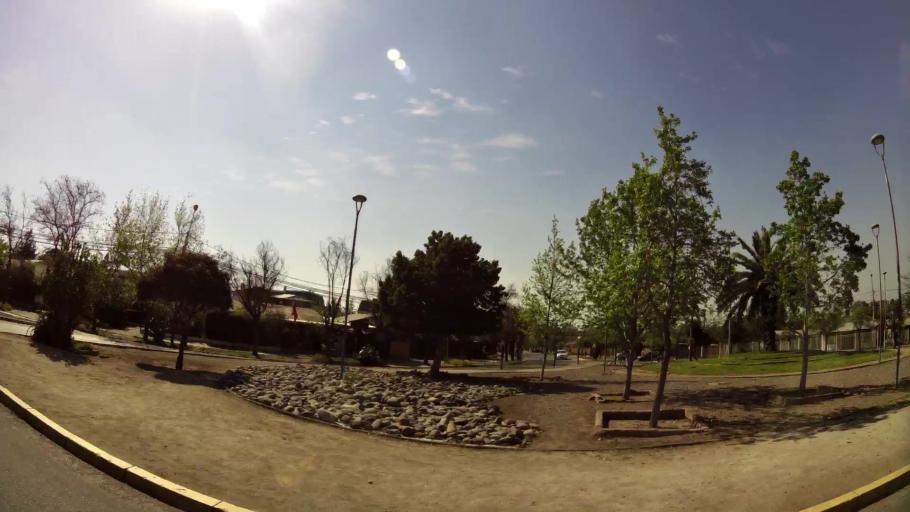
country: CL
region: Santiago Metropolitan
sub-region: Provincia de Santiago
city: La Pintana
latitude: -33.5263
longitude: -70.6074
